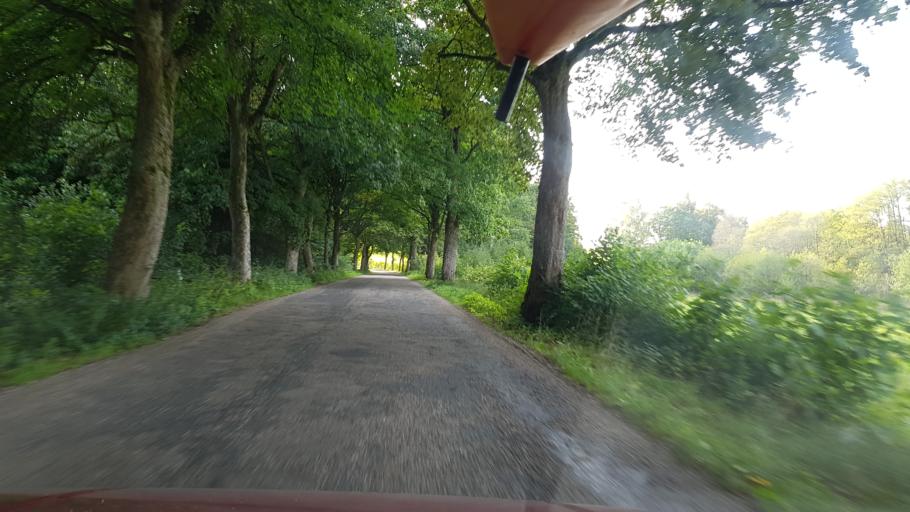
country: PL
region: Pomeranian Voivodeship
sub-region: Powiat bytowski
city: Miastko
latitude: 53.9936
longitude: 16.9151
